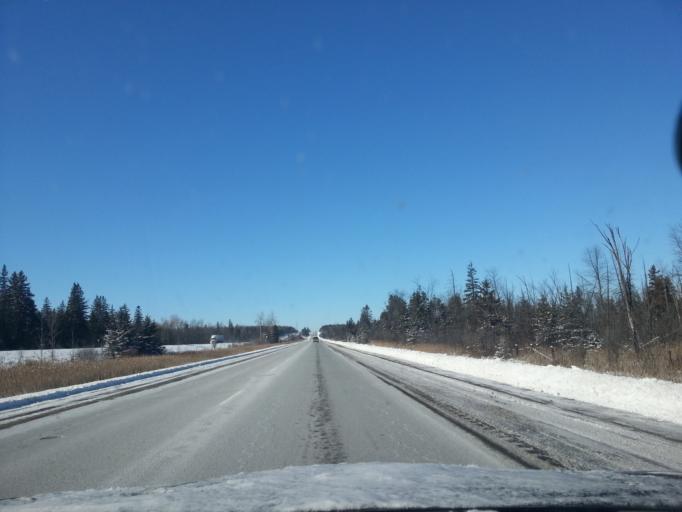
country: CA
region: Ontario
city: Carleton Place
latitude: 45.3236
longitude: -76.1117
